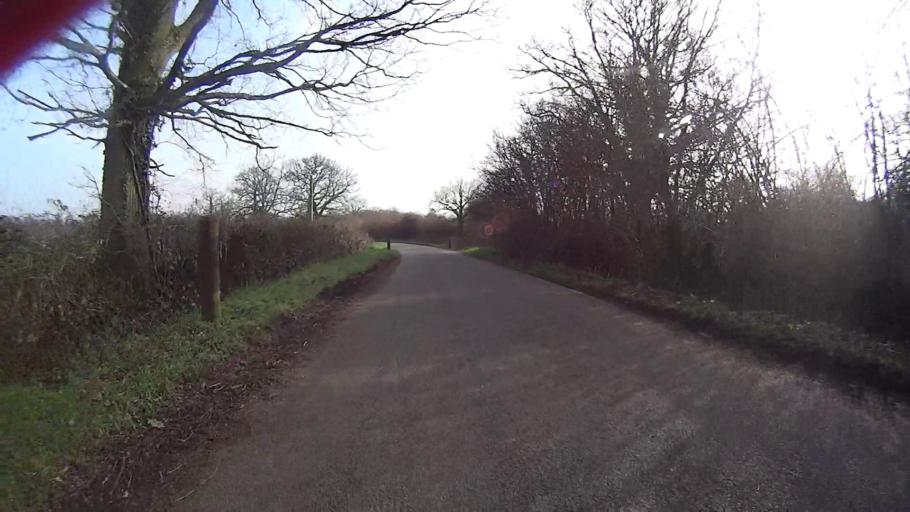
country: GB
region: England
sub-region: Surrey
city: Felbridge
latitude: 51.1661
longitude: -0.0672
